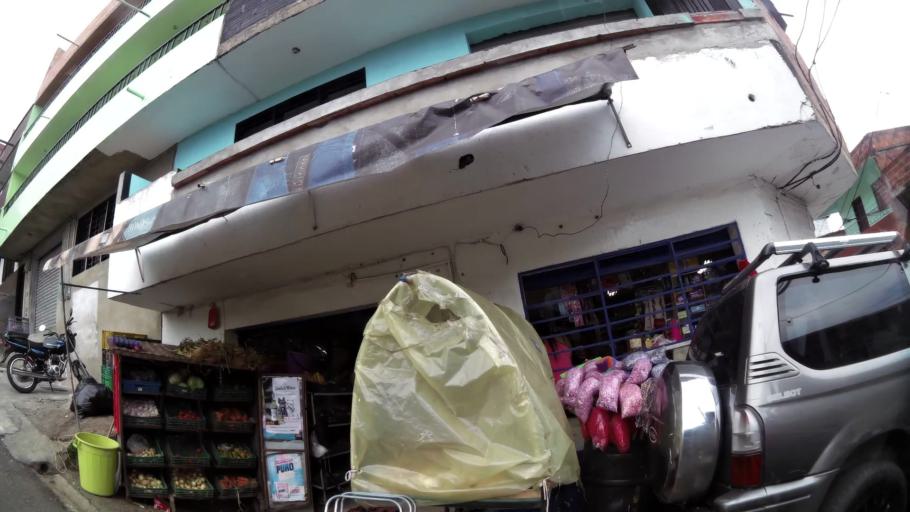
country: CO
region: Antioquia
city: Medellin
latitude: 6.2889
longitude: -75.5480
